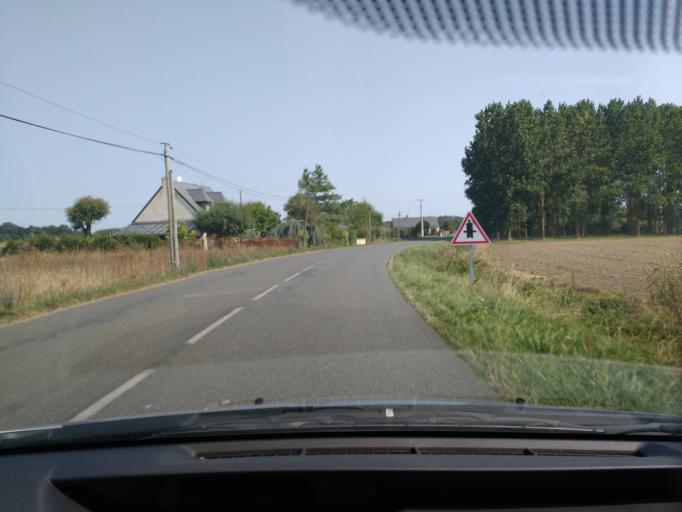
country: FR
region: Pays de la Loire
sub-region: Departement de Maine-et-Loire
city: Baune
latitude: 47.4806
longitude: -0.3162
